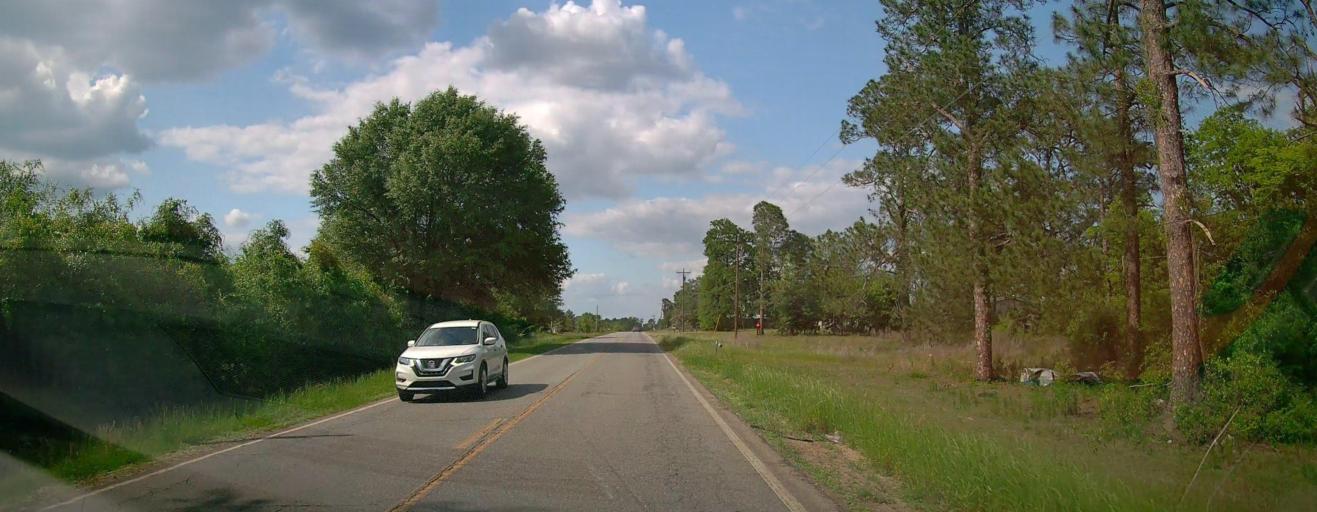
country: US
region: Georgia
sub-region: Laurens County
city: East Dublin
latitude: 32.5881
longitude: -82.8648
